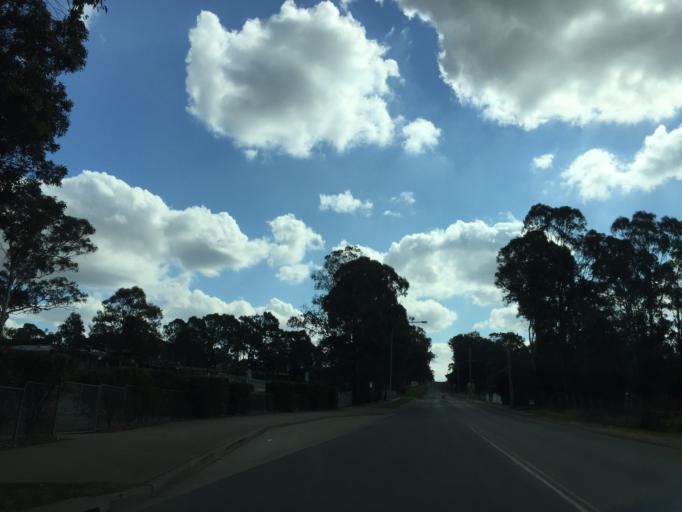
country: AU
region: New South Wales
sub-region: Blacktown
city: Rouse Hill
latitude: -33.6841
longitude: 150.9094
